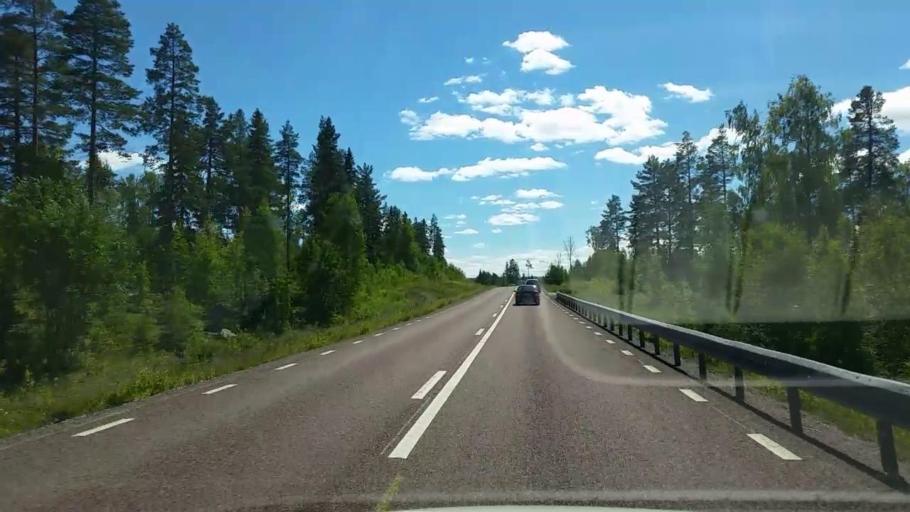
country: SE
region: Gaevleborg
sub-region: Ovanakers Kommun
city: Edsbyn
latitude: 61.2419
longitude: 15.8827
